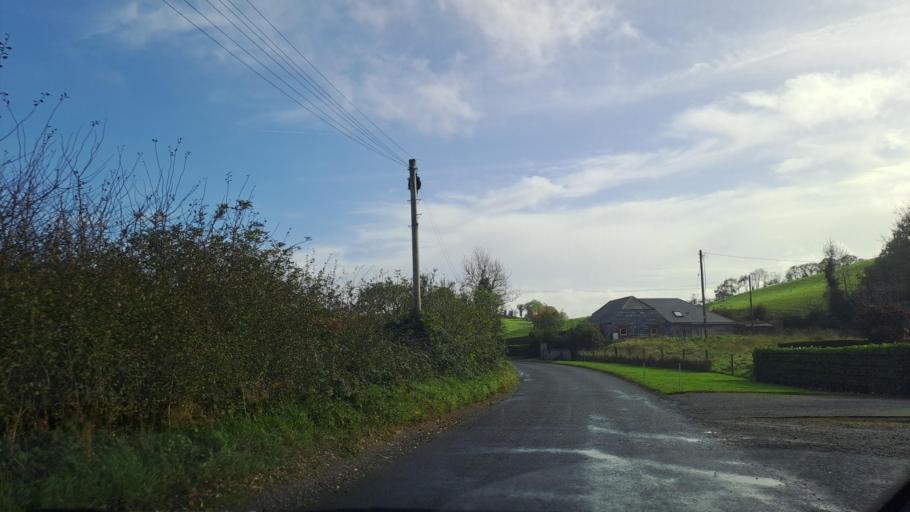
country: IE
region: Ulster
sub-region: County Monaghan
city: Carrickmacross
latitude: 53.8829
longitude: -6.6857
